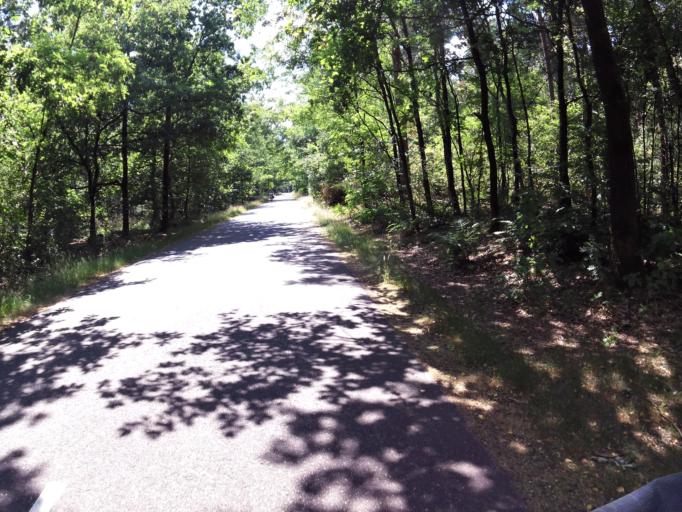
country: NL
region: North Brabant
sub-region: Gemeente Oisterwijk
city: Oisterwijk
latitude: 51.5589
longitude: 5.1987
